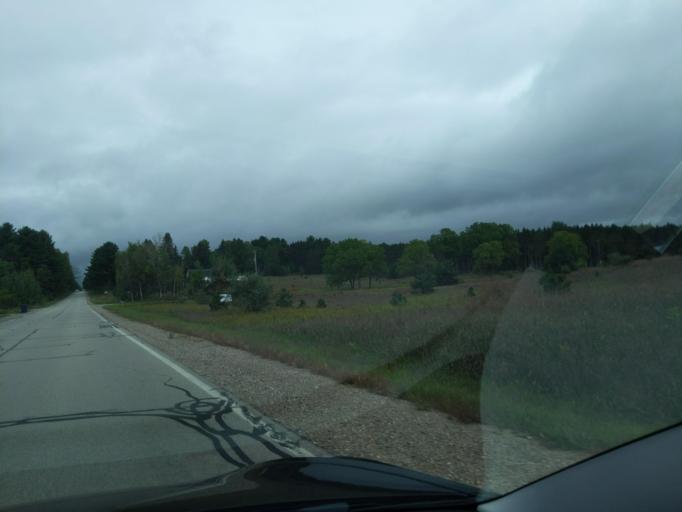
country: US
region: Michigan
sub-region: Grand Traverse County
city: Kingsley
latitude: 44.5974
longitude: -85.3531
